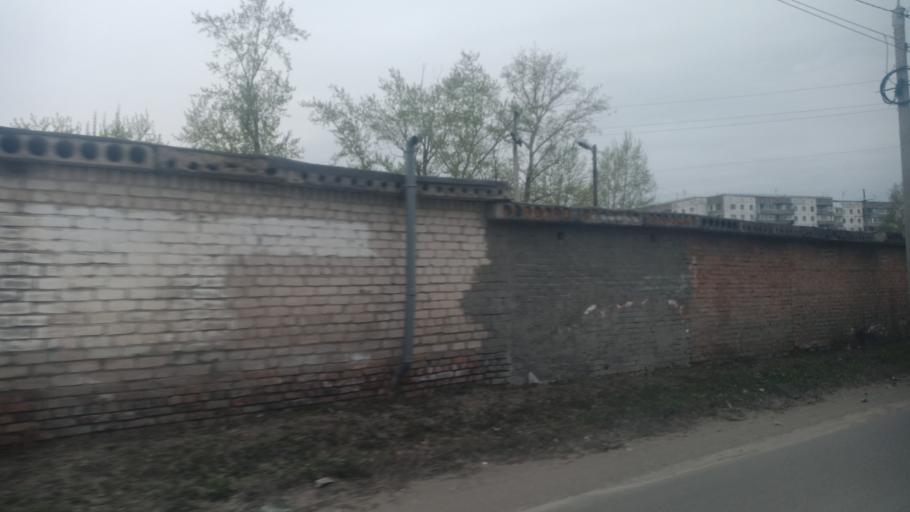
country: RU
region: Altai Krai
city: Yuzhnyy
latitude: 53.2491
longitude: 83.6914
